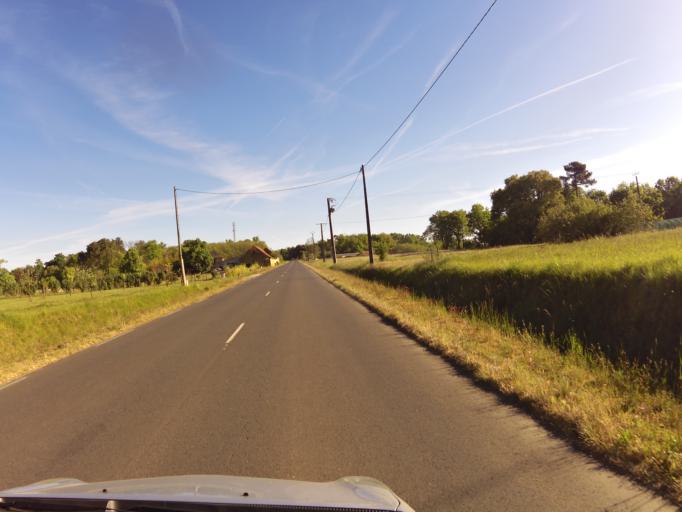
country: FR
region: Aquitaine
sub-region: Departement de la Dordogne
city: Sarlat-la-Caneda
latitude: 44.9868
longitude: 1.2401
